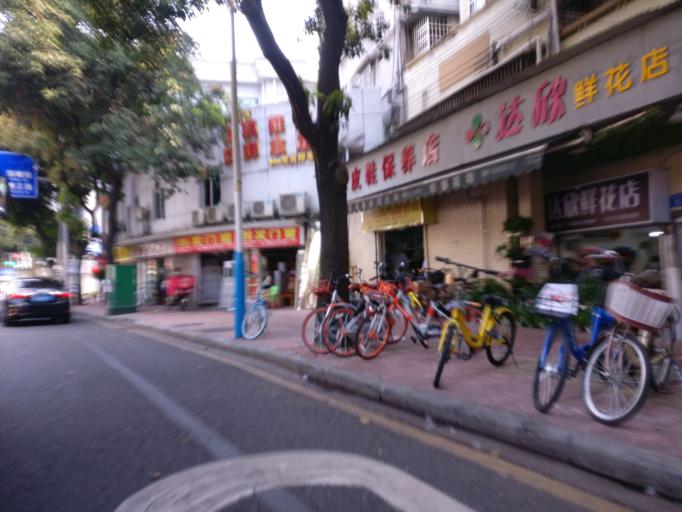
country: CN
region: Guangdong
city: Guangzhou
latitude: 23.1240
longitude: 113.2964
